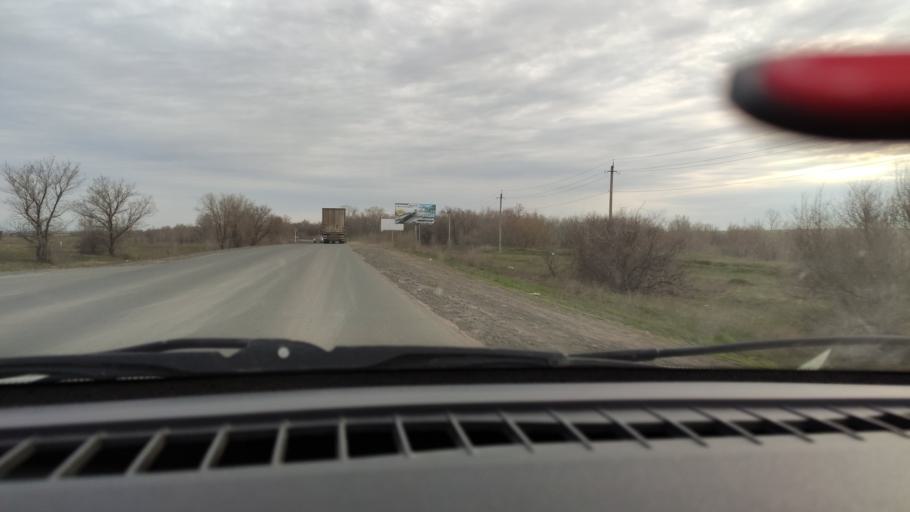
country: RU
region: Orenburg
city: Tatarskaya Kargala
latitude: 51.8969
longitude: 55.1617
